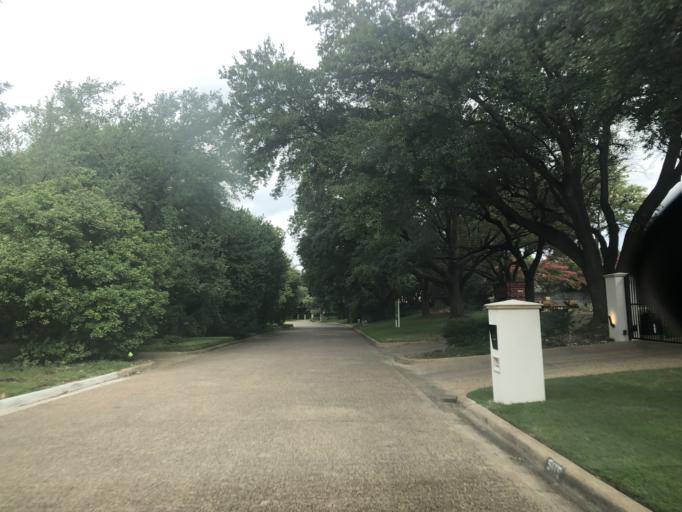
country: US
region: Texas
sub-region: Dallas County
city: University Park
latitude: 32.8676
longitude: -96.8233
